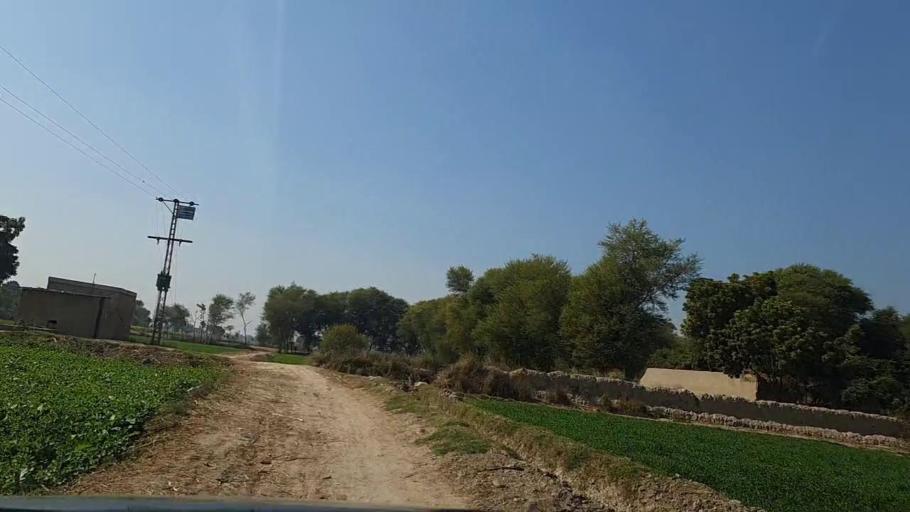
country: PK
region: Sindh
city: Daulatpur
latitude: 26.2890
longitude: 68.0550
